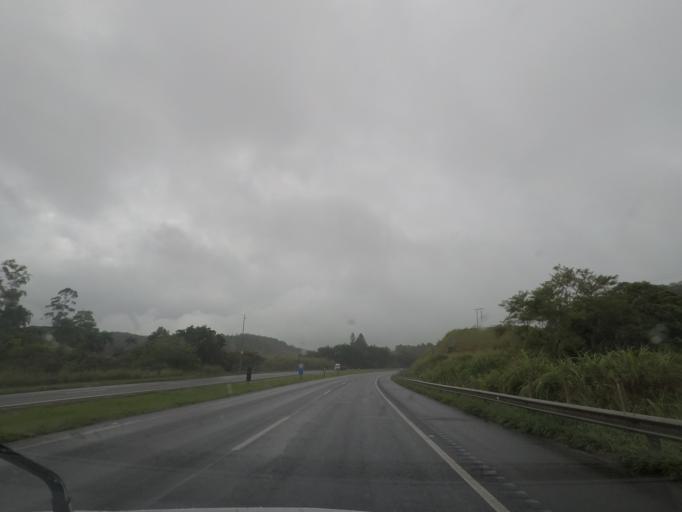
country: BR
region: Sao Paulo
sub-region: Juquia
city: Juquia
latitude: -24.3551
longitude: -47.6747
